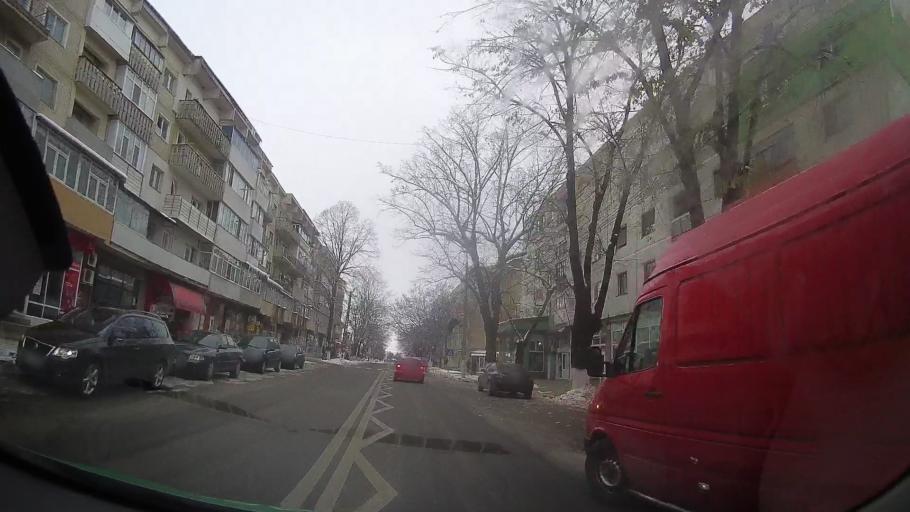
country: RO
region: Vaslui
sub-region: Comuna Negresti
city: Negresti
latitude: 46.8346
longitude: 27.4547
